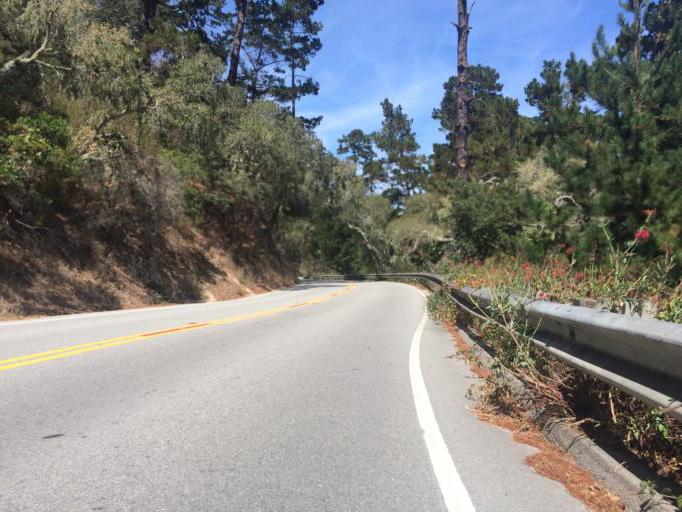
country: US
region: California
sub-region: Monterey County
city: Carmel-by-the-Sea
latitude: 36.5625
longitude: -121.9255
